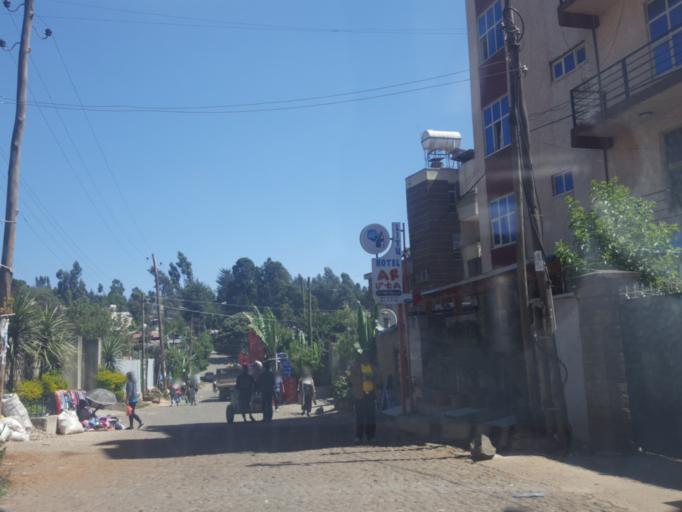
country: ET
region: Adis Abeba
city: Addis Ababa
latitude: 9.0607
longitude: 38.7367
